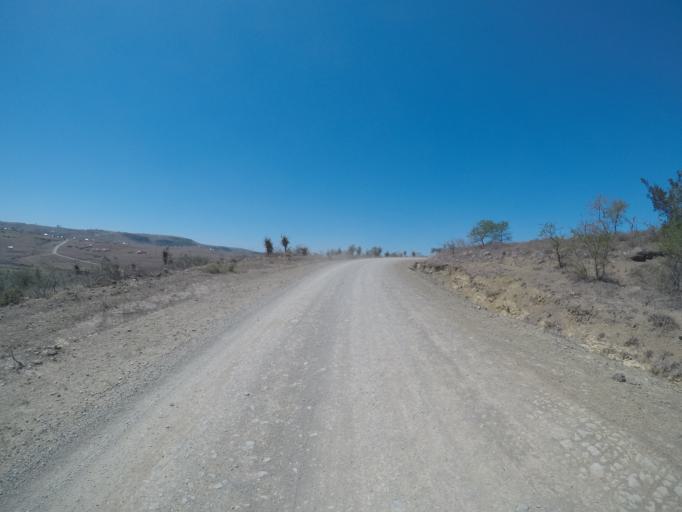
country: ZA
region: Eastern Cape
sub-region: OR Tambo District Municipality
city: Mthatha
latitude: -31.8728
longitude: 28.8705
